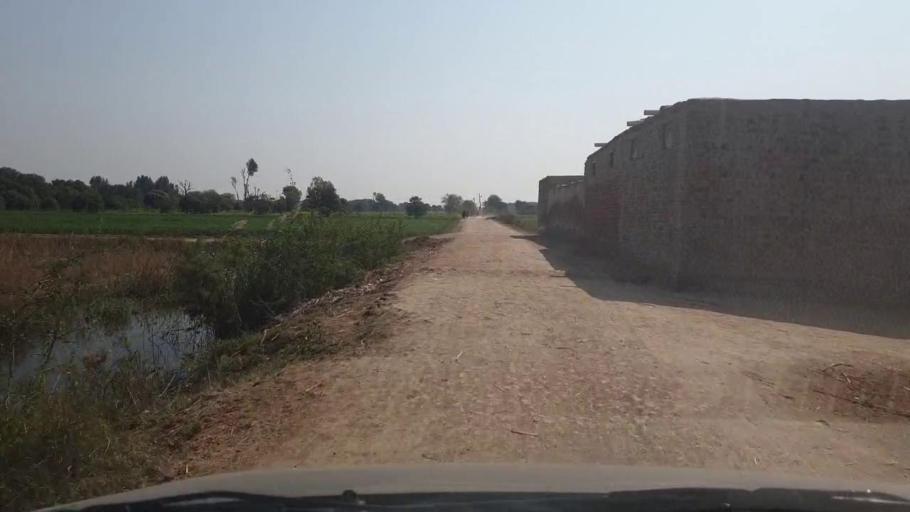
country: PK
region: Sindh
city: Mirwah Gorchani
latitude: 25.2515
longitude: 69.1218
